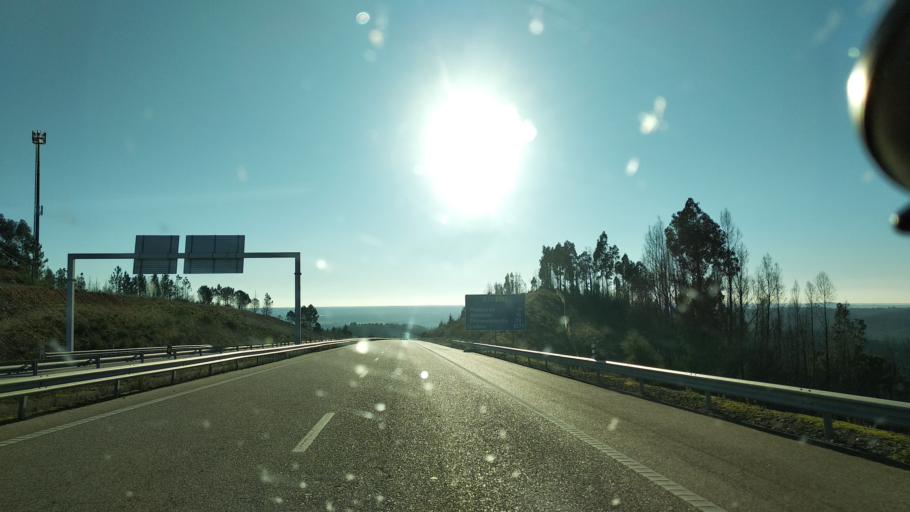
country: PT
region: Santarem
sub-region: Macao
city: Macao
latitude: 39.5064
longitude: -8.0224
